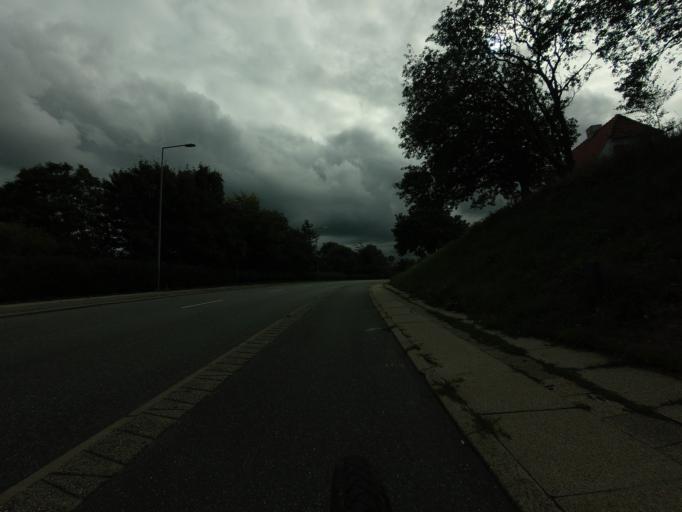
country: DK
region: North Denmark
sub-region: Hjorring Kommune
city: Hjorring
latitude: 57.4720
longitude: 9.9904
